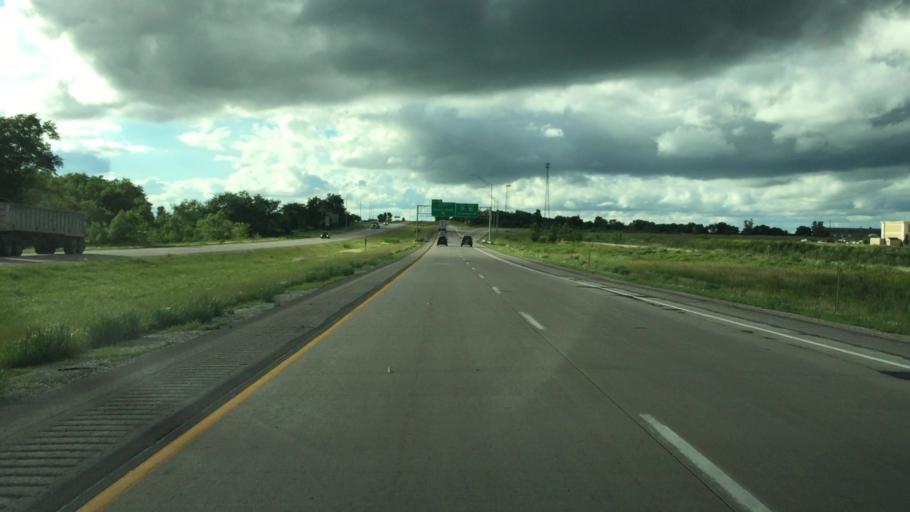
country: US
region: Iowa
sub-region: Polk County
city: Altoona
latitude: 41.6529
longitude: -93.5164
